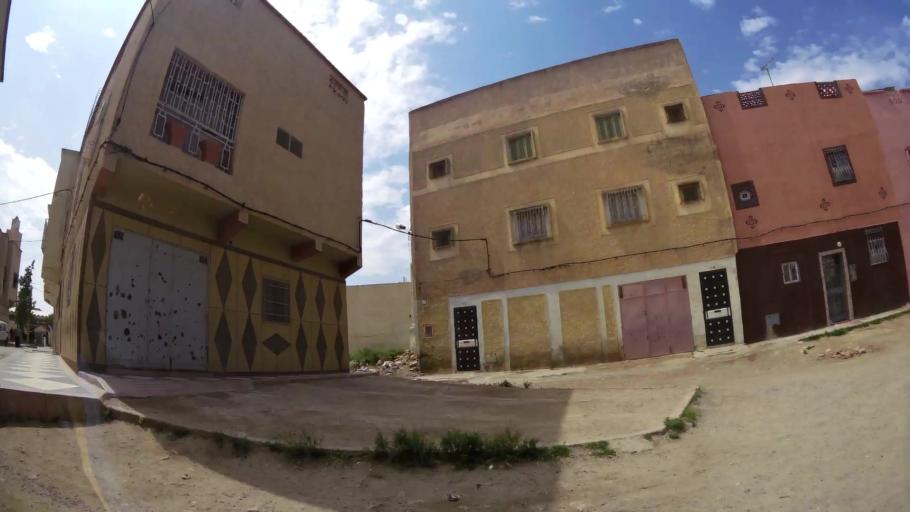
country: MA
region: Oriental
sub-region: Oujda-Angad
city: Oujda
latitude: 34.6861
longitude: -1.9030
